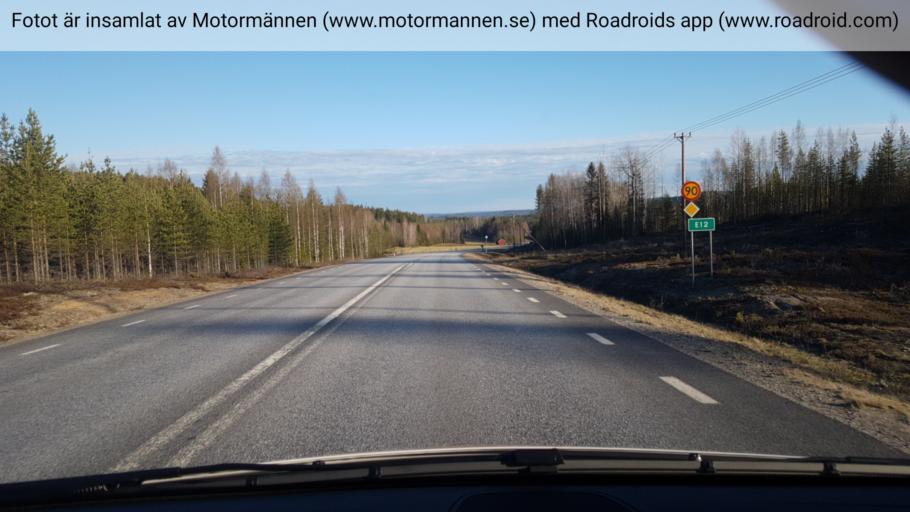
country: SE
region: Vaesterbotten
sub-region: Vannas Kommun
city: Vaennaes
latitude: 64.0297
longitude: 19.6921
